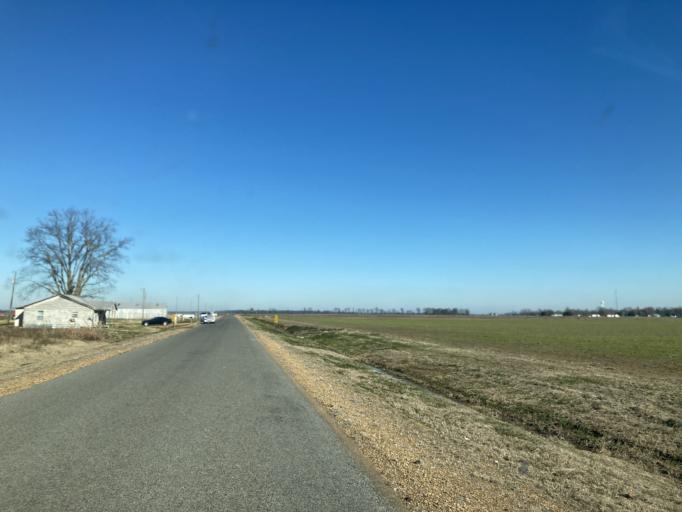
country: US
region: Mississippi
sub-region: Yazoo County
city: Yazoo City
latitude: 32.9687
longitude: -90.6054
